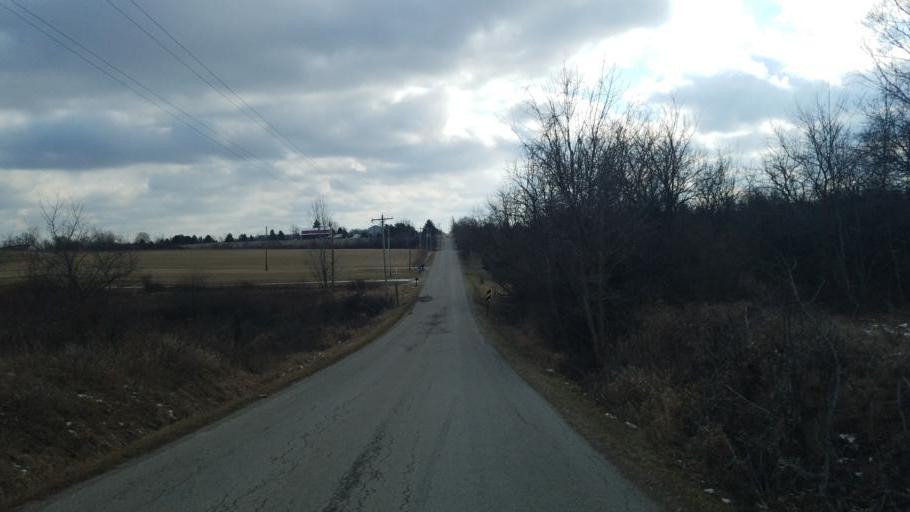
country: US
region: Ohio
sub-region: Crawford County
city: Galion
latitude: 40.6303
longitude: -82.7471
